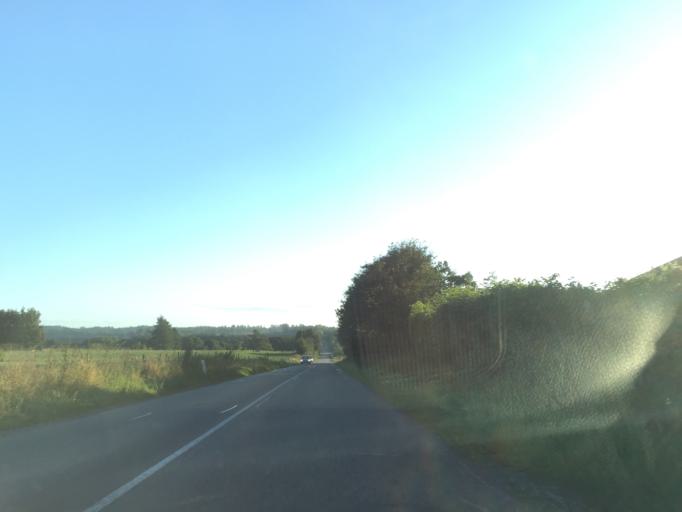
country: DK
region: Central Jutland
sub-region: Viborg Kommune
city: Bjerringbro
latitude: 56.3437
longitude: 9.6495
